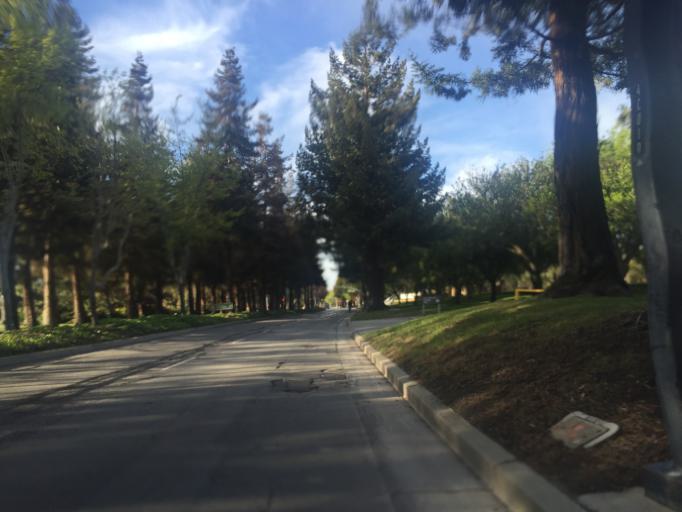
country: US
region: California
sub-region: Santa Clara County
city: Mountain View
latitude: 37.4218
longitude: -122.0780
